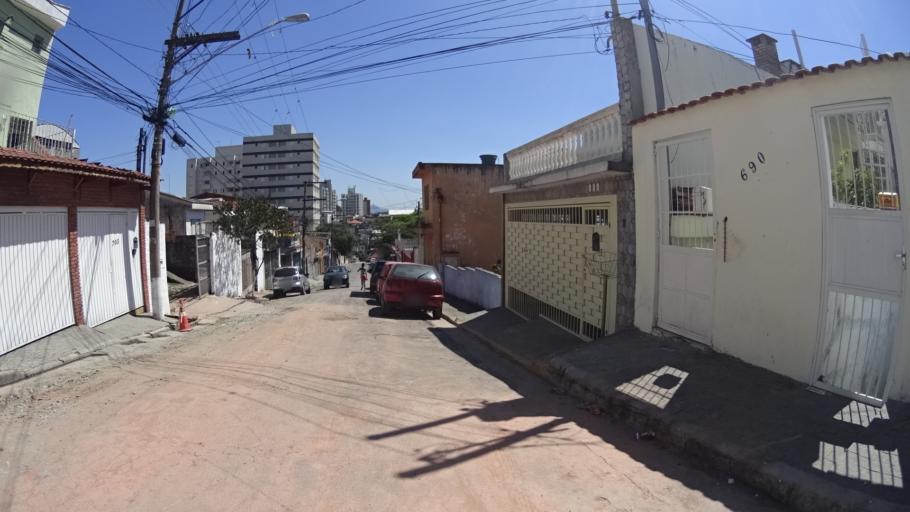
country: BR
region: Sao Paulo
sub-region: Sao Paulo
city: Sao Paulo
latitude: -23.4867
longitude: -46.6700
